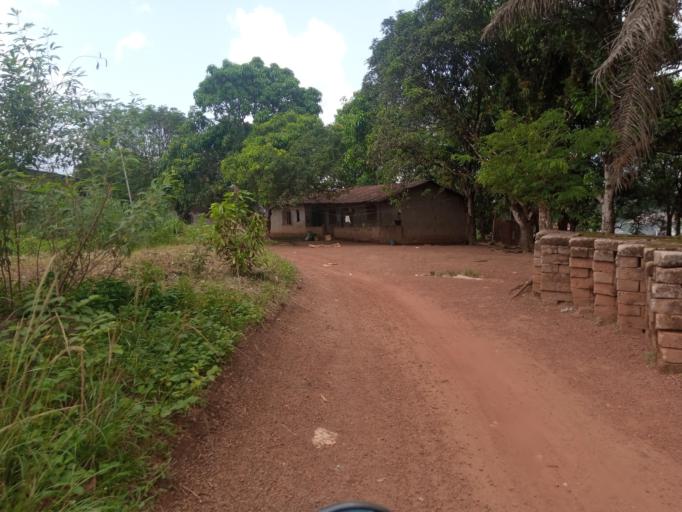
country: SL
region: Southern Province
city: Baoma
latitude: 7.9823
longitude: -11.7283
